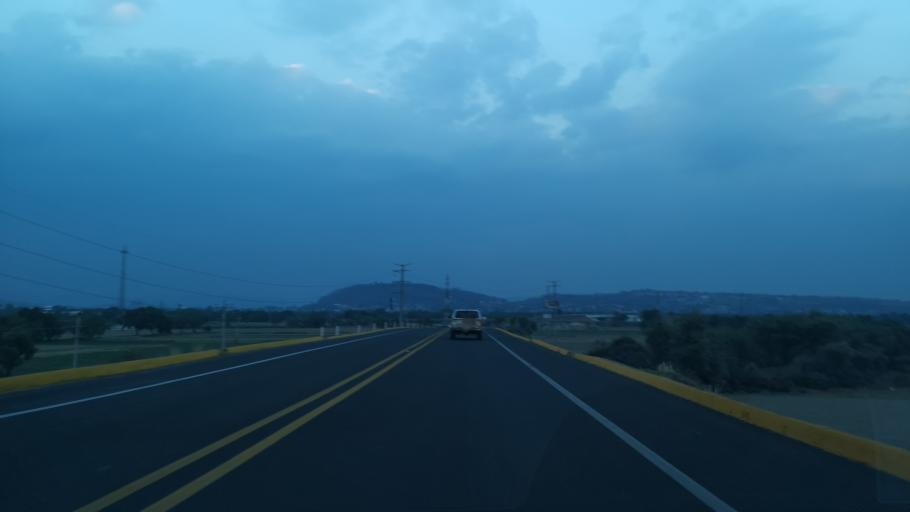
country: MX
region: Puebla
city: Santa Ana Xalmimilulco
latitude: 19.2082
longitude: -98.3606
